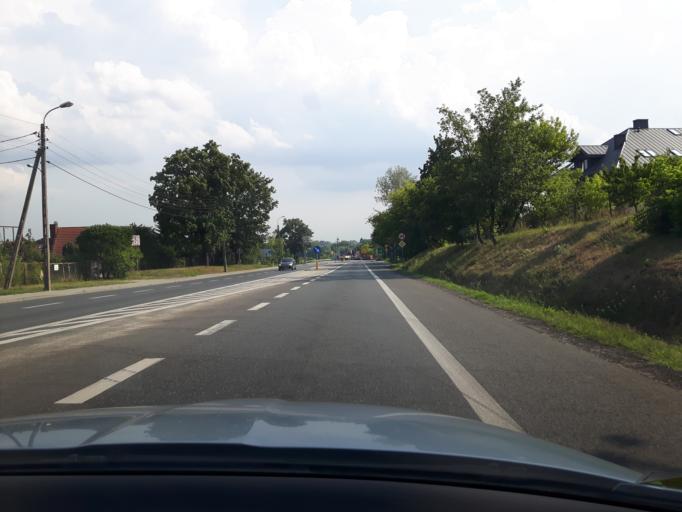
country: PL
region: Masovian Voivodeship
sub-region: Powiat nowodworski
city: Nowy Dwor Mazowiecki
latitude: 52.4429
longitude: 20.6963
